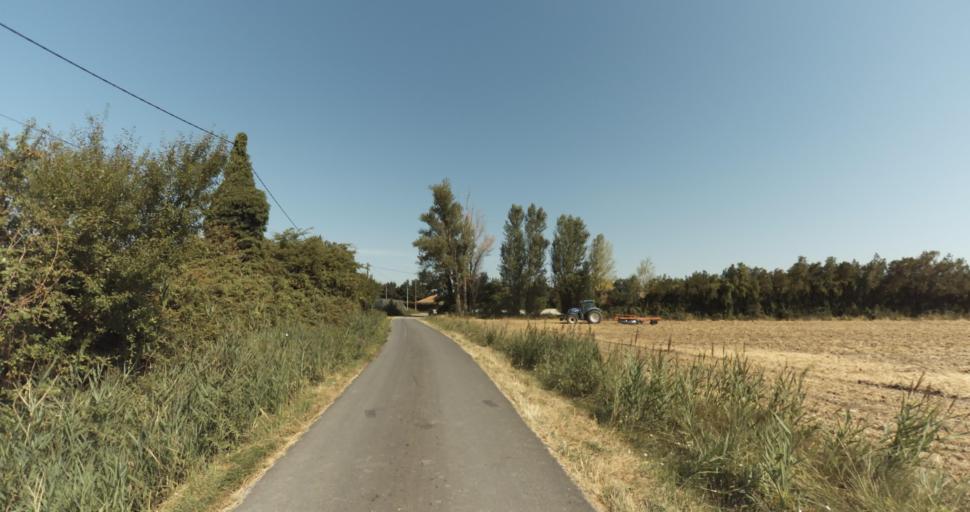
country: FR
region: Provence-Alpes-Cote d'Azur
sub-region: Departement du Vaucluse
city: Althen-des-Paluds
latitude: 44.0035
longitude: 4.9880
